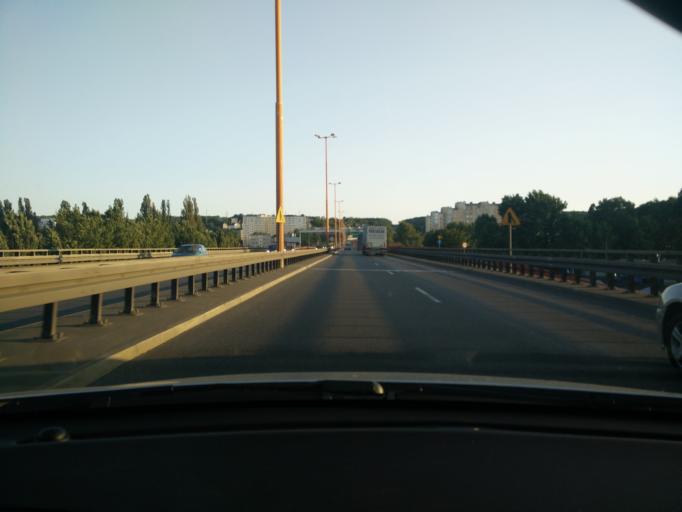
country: PL
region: Pomeranian Voivodeship
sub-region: Gdynia
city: Pogorze
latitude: 54.5374
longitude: 18.4932
